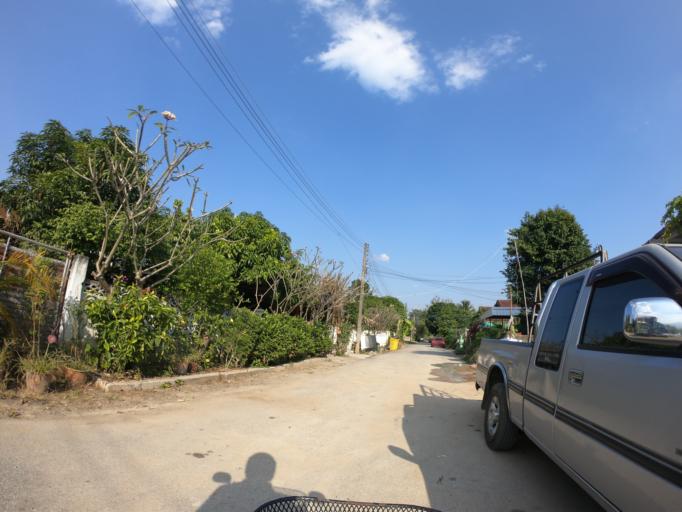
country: TH
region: Chiang Mai
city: Chiang Mai
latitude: 18.8324
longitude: 98.9859
